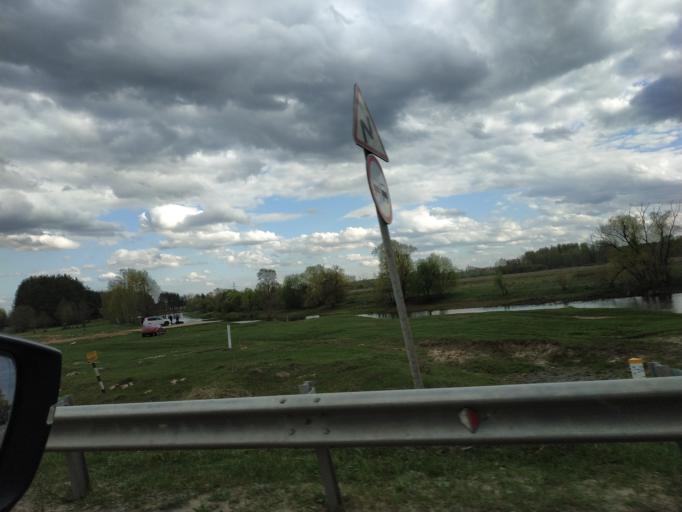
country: RU
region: Moskovskaya
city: Pavlovskiy Posad
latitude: 55.8025
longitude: 38.6706
